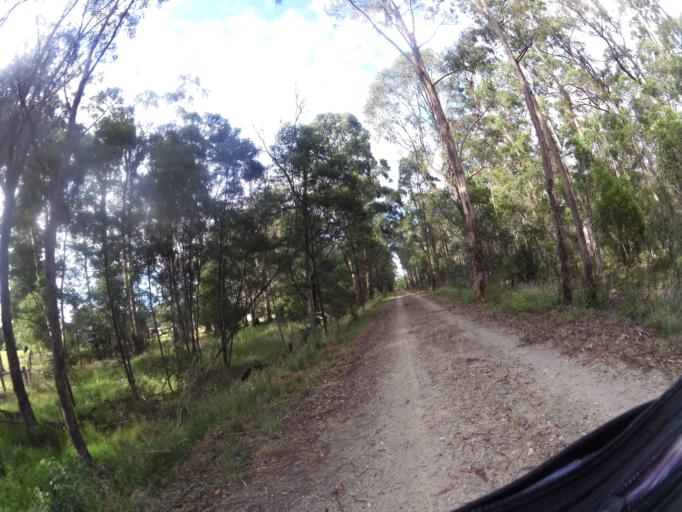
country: AU
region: Victoria
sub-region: East Gippsland
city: Lakes Entrance
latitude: -37.7385
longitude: 148.4202
